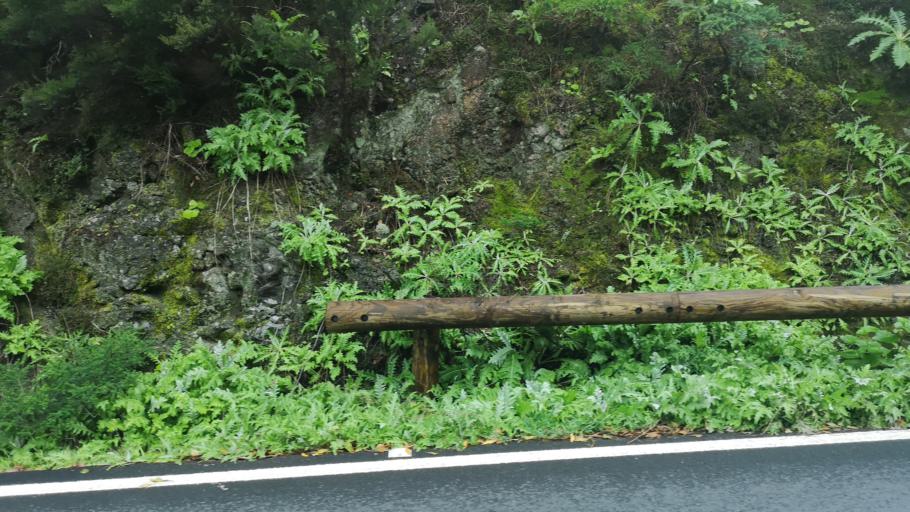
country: ES
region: Canary Islands
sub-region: Provincia de Santa Cruz de Tenerife
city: Alajero
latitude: 28.1070
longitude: -17.2377
